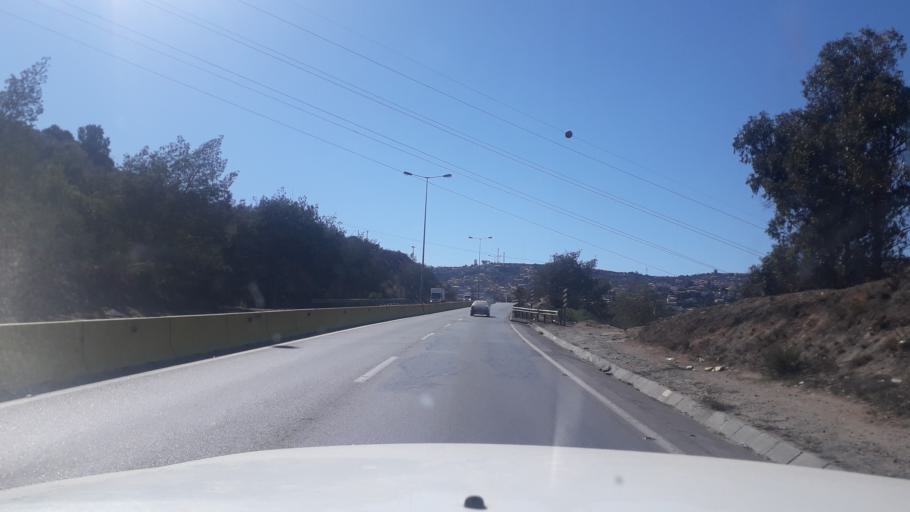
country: CL
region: Valparaiso
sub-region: Provincia de Valparaiso
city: Vina del Mar
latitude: -33.0313
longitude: -71.5004
